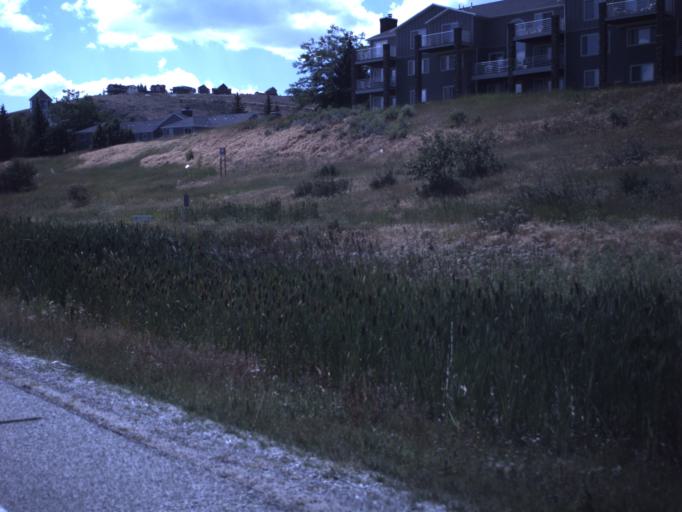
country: US
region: Idaho
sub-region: Bear Lake County
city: Paris
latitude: 41.9638
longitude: -111.4000
